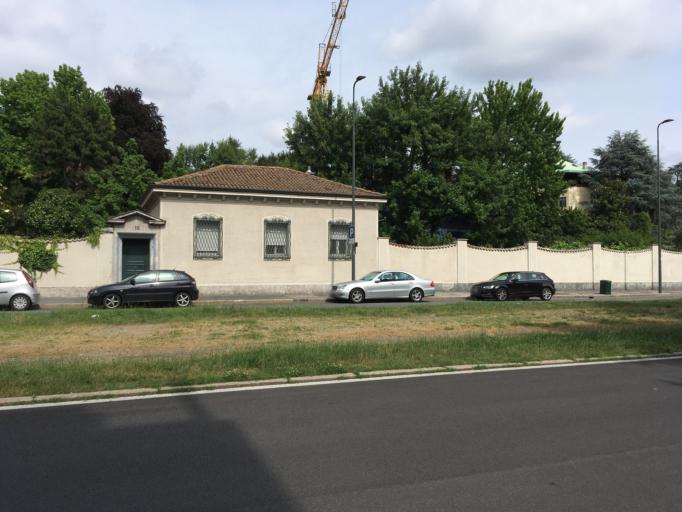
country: IT
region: Lombardy
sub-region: Citta metropolitana di Milano
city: Romano Banco
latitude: 45.4777
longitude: 9.1313
